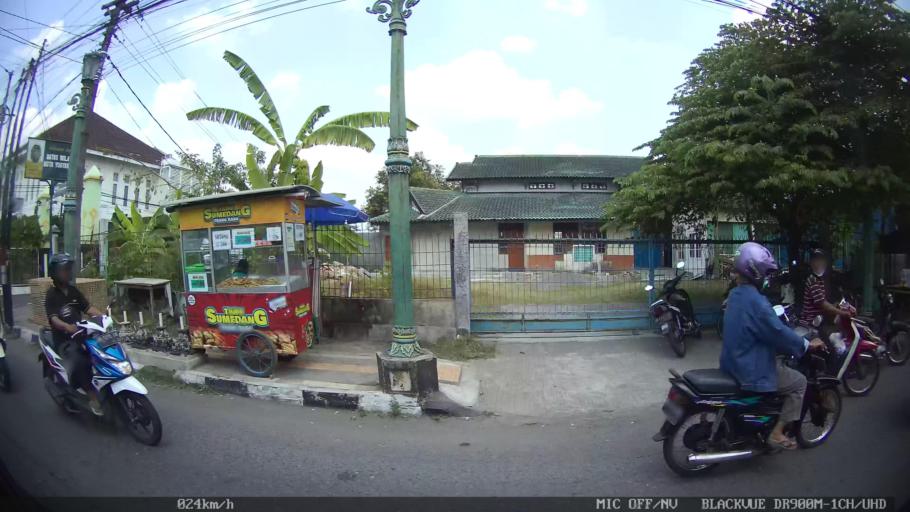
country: ID
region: Daerah Istimewa Yogyakarta
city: Yogyakarta
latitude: -7.8281
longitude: 110.4047
